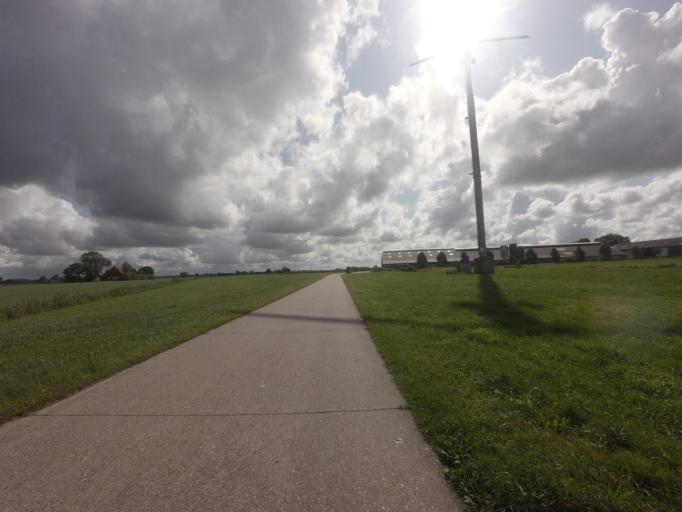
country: NL
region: Friesland
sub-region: Sudwest Fryslan
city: Scharnegoutum
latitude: 53.0729
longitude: 5.6372
